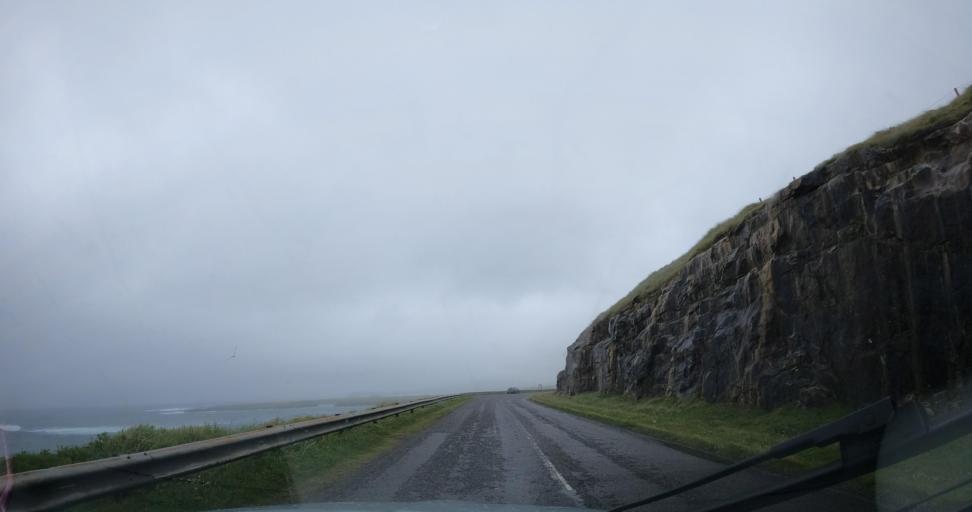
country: GB
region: Scotland
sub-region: Eilean Siar
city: Barra
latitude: 56.9775
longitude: -7.5176
